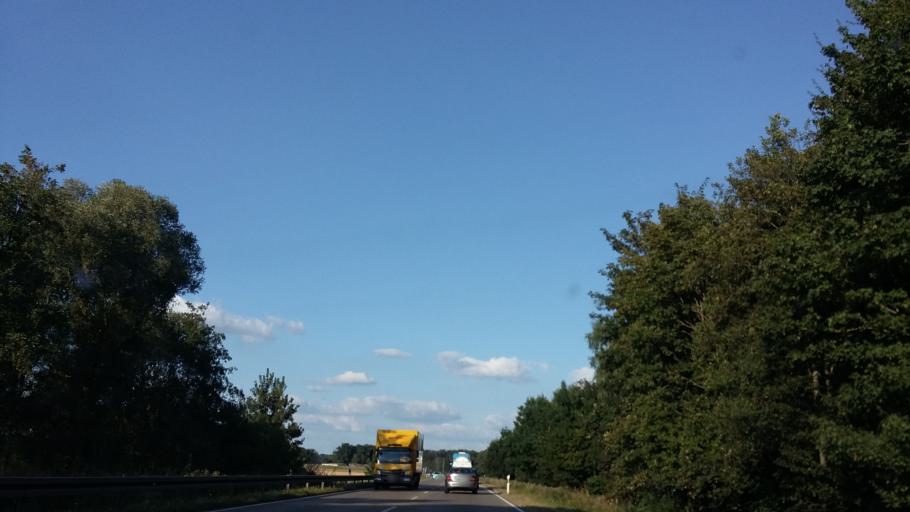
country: DE
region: Bavaria
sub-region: Swabia
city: Holzheim
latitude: 48.4010
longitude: 10.0725
